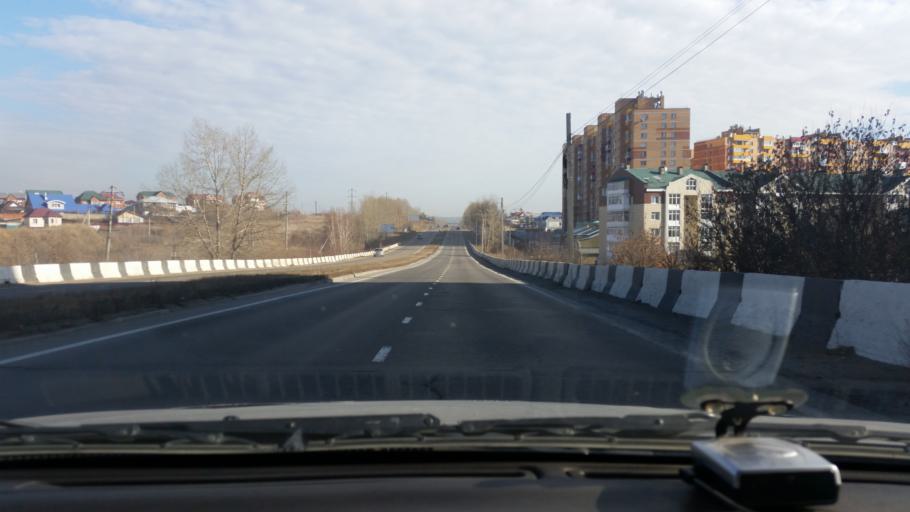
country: RU
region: Irkutsk
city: Dzerzhinsk
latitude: 52.2598
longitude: 104.3595
